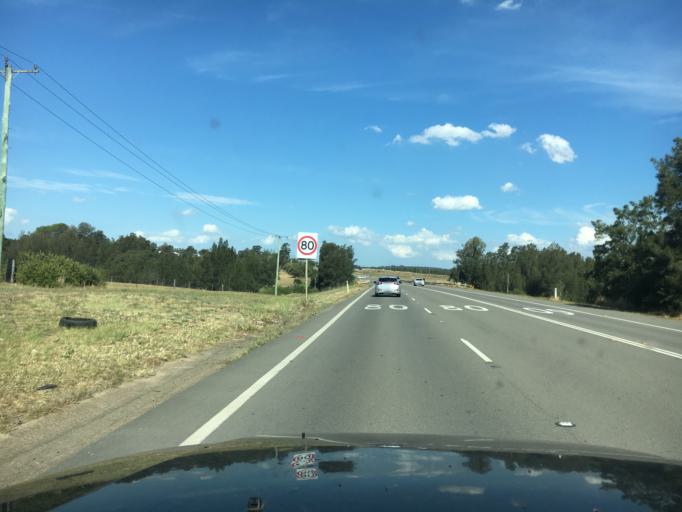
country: AU
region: New South Wales
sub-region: Cessnock
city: Branxton
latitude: -32.6593
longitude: 151.3640
